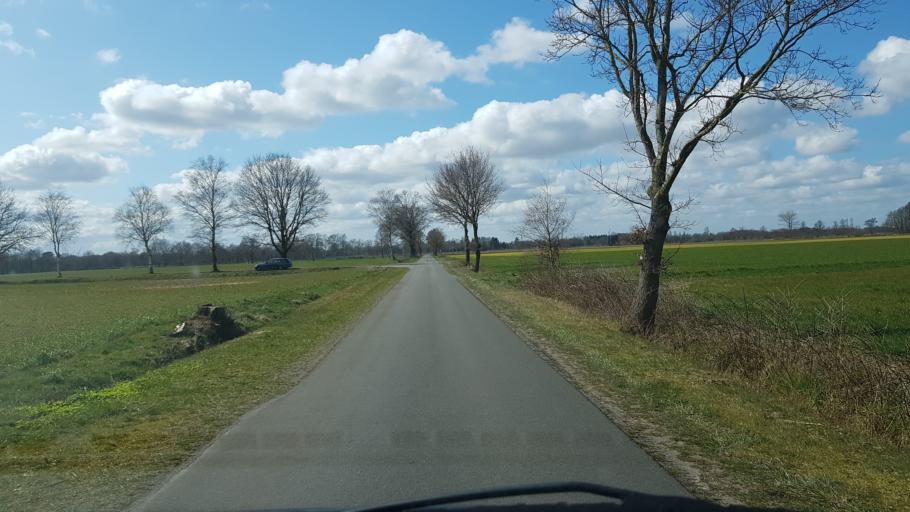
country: DE
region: Lower Saxony
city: Westerstede
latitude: 53.1756
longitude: 7.9181
